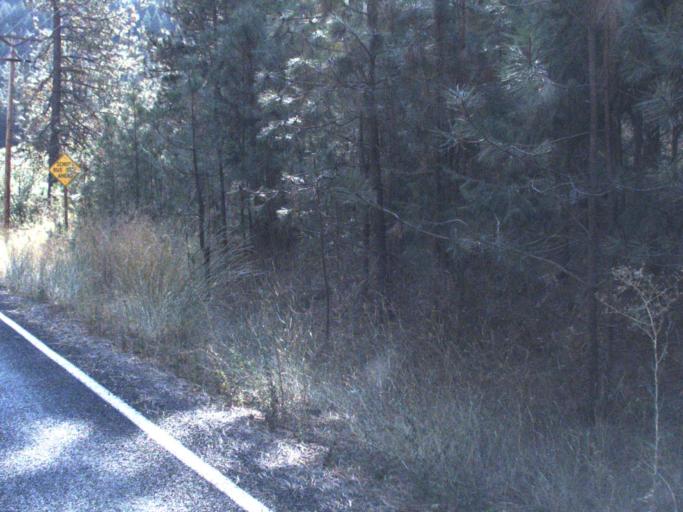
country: US
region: Washington
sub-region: Spokane County
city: Deer Park
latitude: 47.8942
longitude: -117.6620
